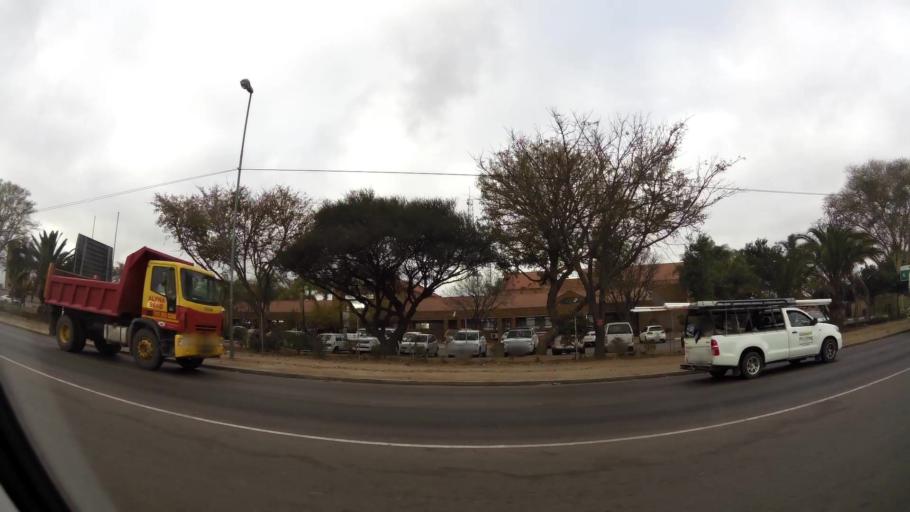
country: ZA
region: Limpopo
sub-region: Capricorn District Municipality
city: Polokwane
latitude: -23.8761
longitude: 29.4417
